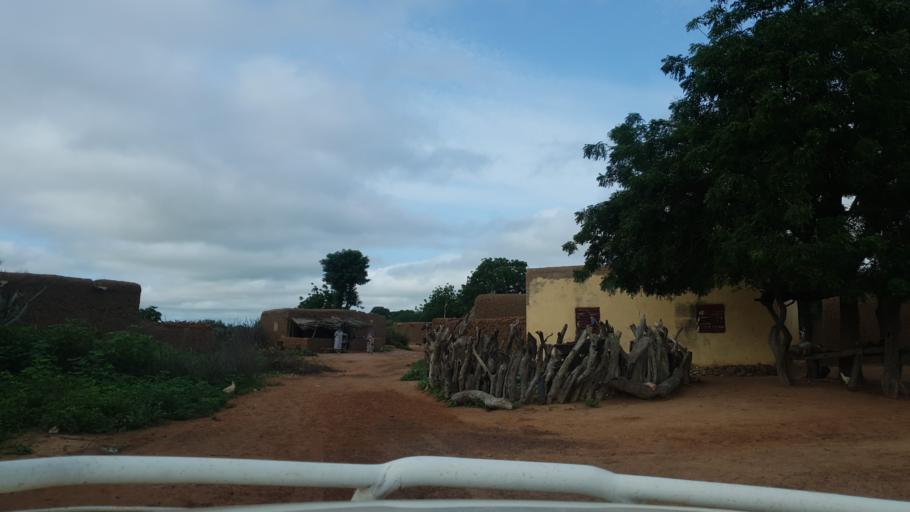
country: ML
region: Segou
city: Baroueli
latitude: 13.5068
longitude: -6.9003
